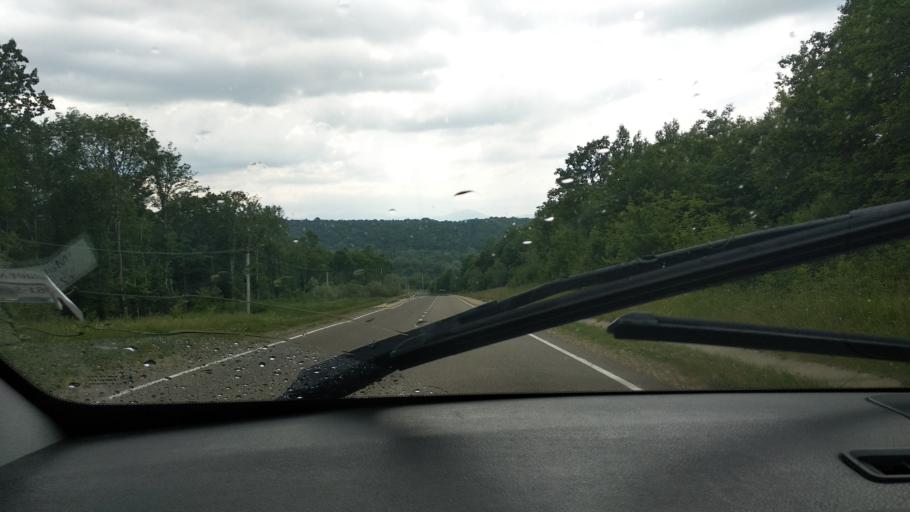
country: RU
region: Krasnodarskiy
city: Neftegorsk
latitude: 44.2737
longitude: 39.9313
